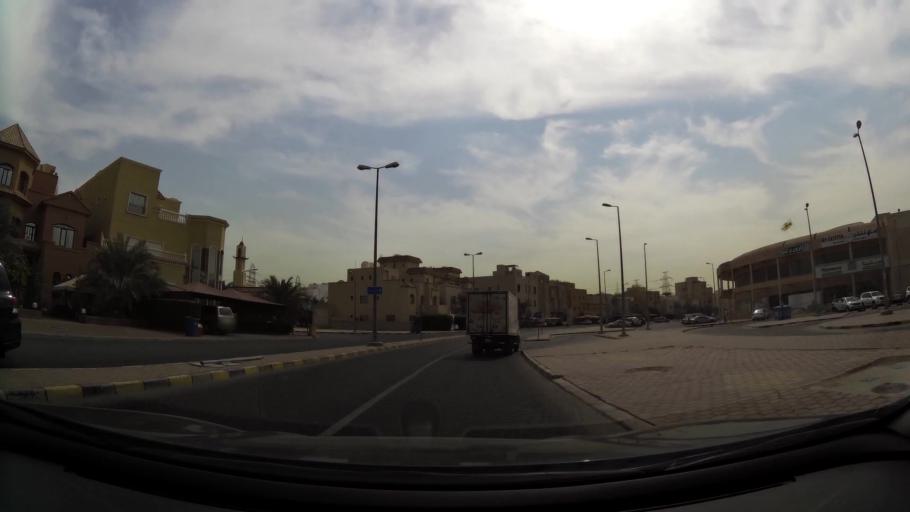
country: KW
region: Mubarak al Kabir
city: Sabah as Salim
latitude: 29.2711
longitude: 48.0341
